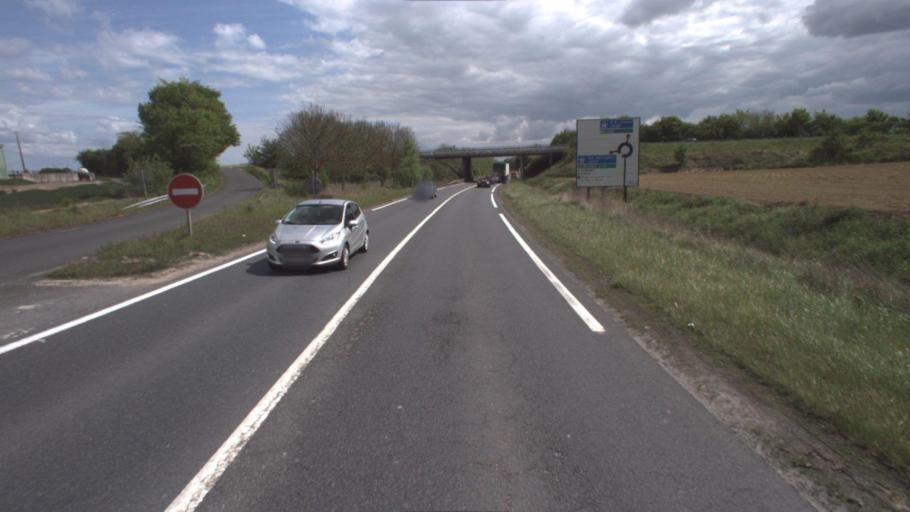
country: FR
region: Ile-de-France
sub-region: Departement de Seine-et-Marne
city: Cregy-les-Meaux
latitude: 48.9905
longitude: 2.8672
